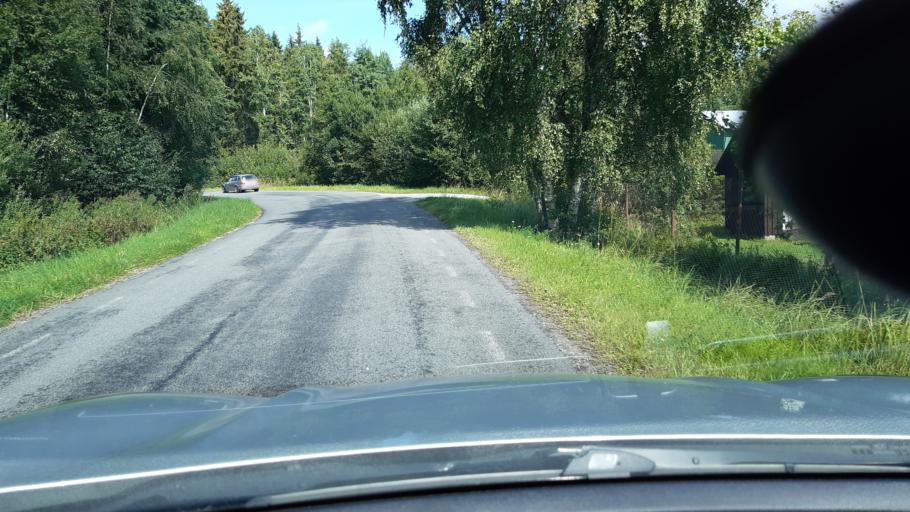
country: EE
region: Raplamaa
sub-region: Rapla vald
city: Rapla
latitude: 59.0116
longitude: 24.8131
